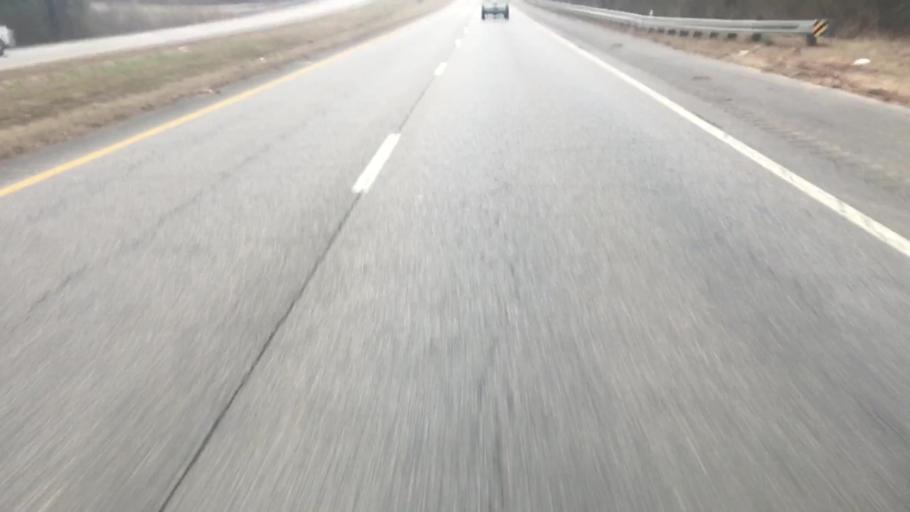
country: US
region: Alabama
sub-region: Walker County
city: Sumiton
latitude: 33.7177
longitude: -86.9987
